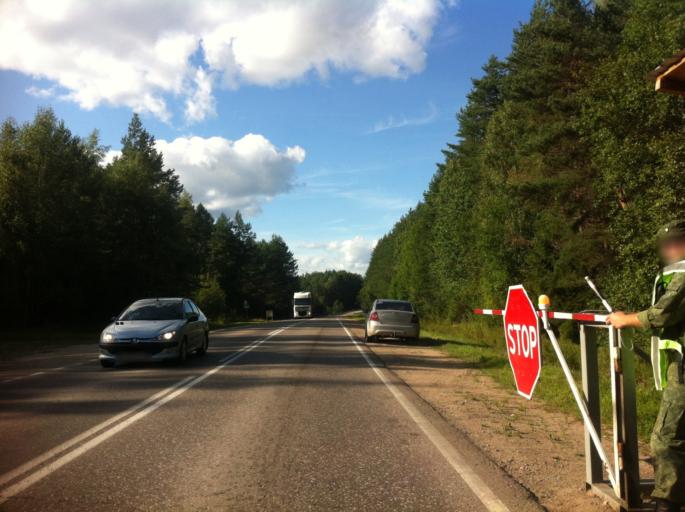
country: RU
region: Pskov
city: Pechory
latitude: 57.7994
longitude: 27.6615
